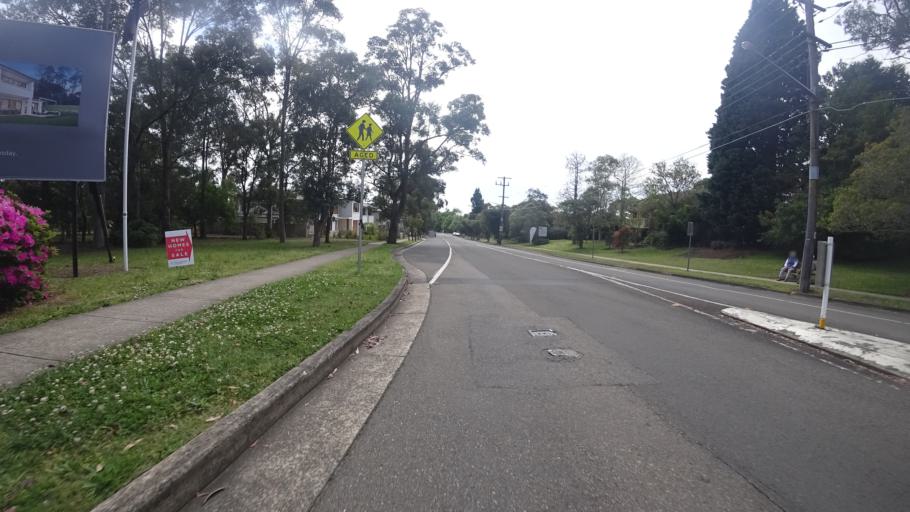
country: AU
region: New South Wales
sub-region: City of Sydney
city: North Turramurra
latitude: -33.6979
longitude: 151.1489
